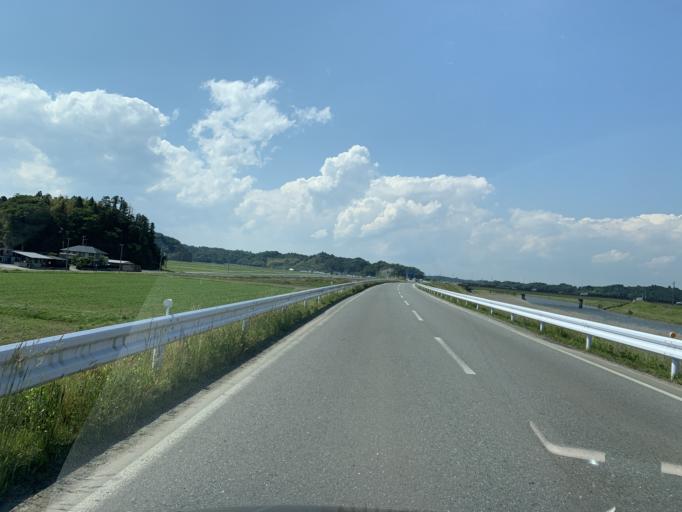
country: JP
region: Miyagi
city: Yamoto
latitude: 38.3922
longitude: 141.1576
